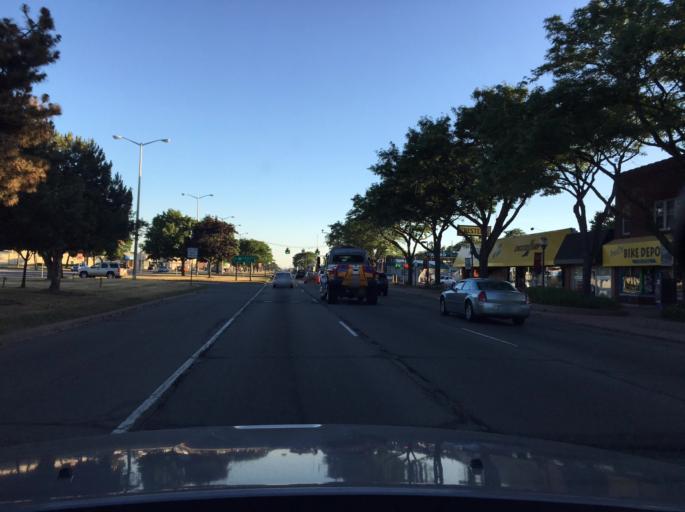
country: US
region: Michigan
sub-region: Macomb County
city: Roseville
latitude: 42.5032
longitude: -82.9329
